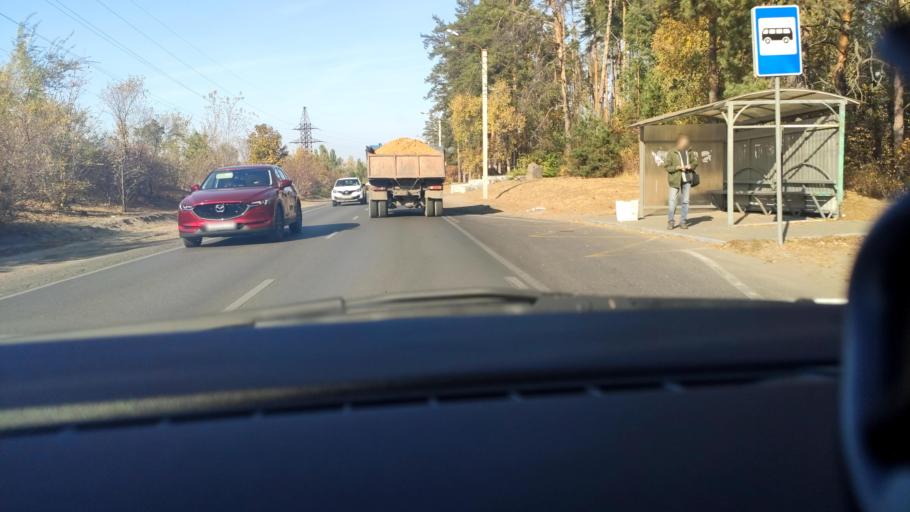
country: RU
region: Voronezj
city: Pridonskoy
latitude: 51.6315
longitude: 39.0822
